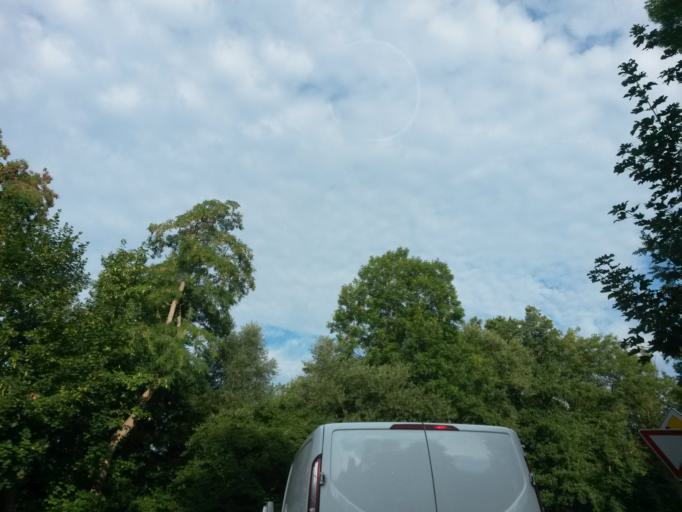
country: DE
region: North Rhine-Westphalia
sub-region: Regierungsbezirk Koln
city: Rosrath
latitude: 50.8889
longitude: 7.1878
